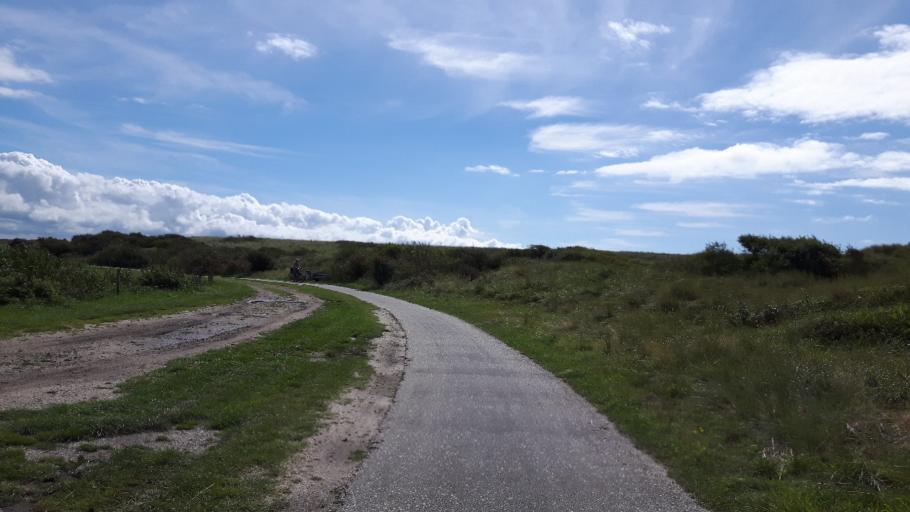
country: NL
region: Friesland
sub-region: Gemeente Ameland
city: Hollum
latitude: 53.4371
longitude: 5.6246
